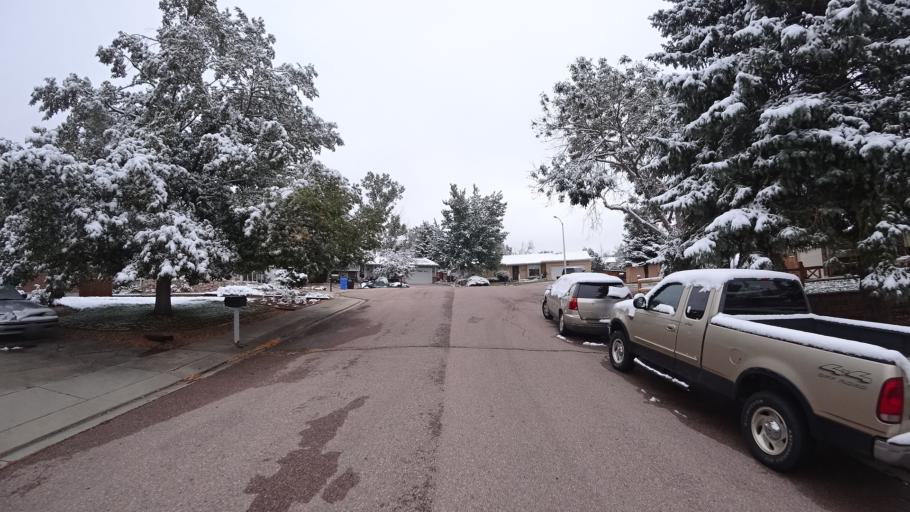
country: US
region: Colorado
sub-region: El Paso County
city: Colorado Springs
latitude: 38.9203
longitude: -104.7802
